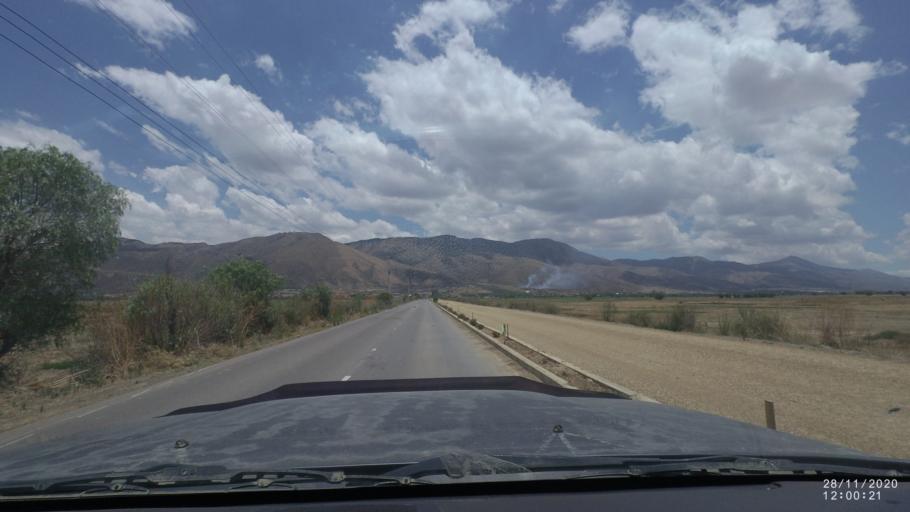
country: BO
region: Cochabamba
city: Tarata
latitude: -17.5590
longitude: -66.0084
